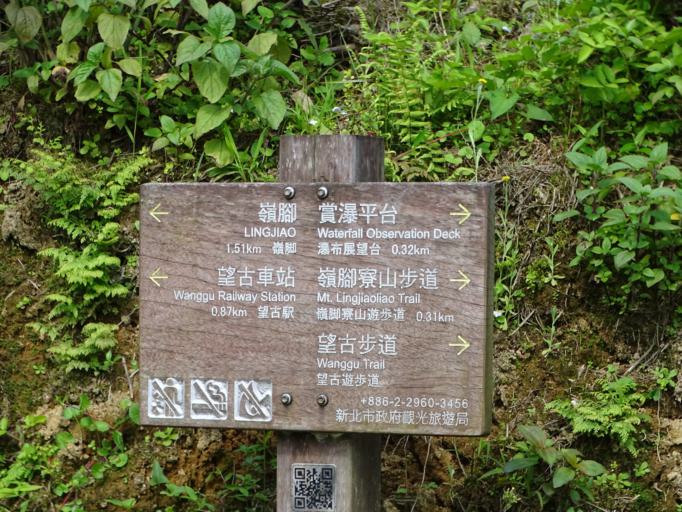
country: TW
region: Taiwan
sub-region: Keelung
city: Keelung
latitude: 25.0358
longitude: 121.7574
